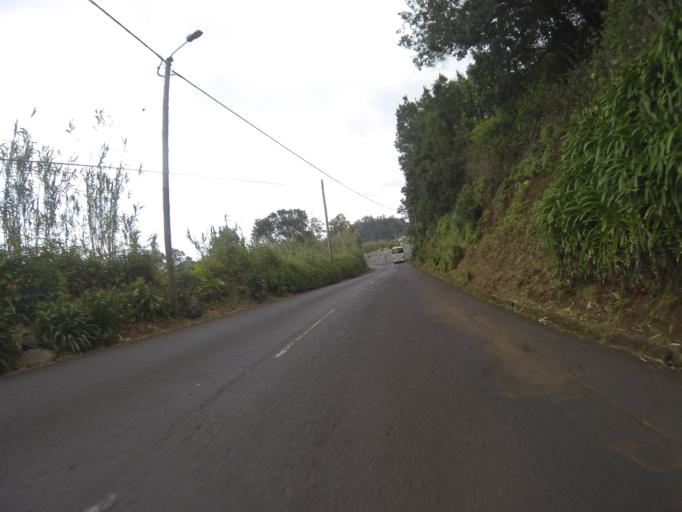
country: PT
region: Madeira
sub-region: Porto Moniz
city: Porto Moniz
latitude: 32.8610
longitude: -17.1754
